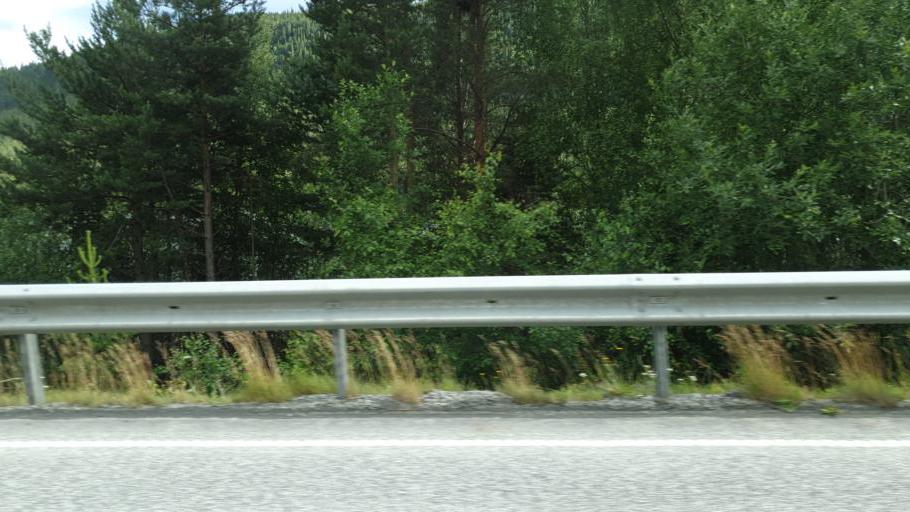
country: NO
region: Oppland
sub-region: Vaga
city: Vagamo
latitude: 61.8745
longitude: 9.1672
